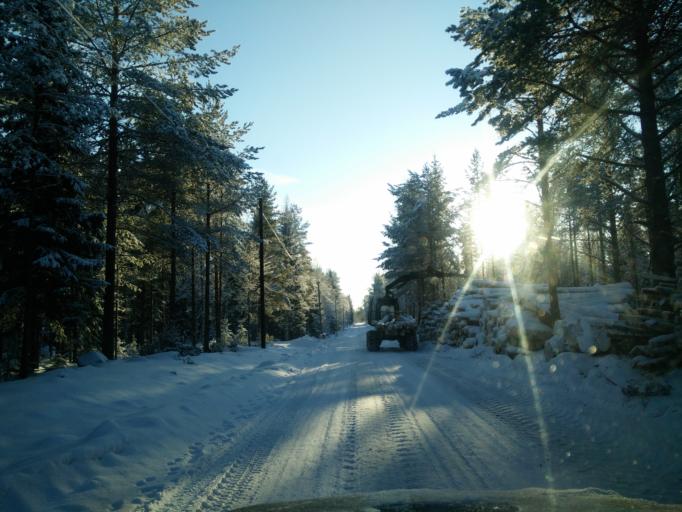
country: SE
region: Vaesternorrland
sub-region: Sundsvalls Kommun
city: Njurundabommen
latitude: 62.2148
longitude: 17.4936
